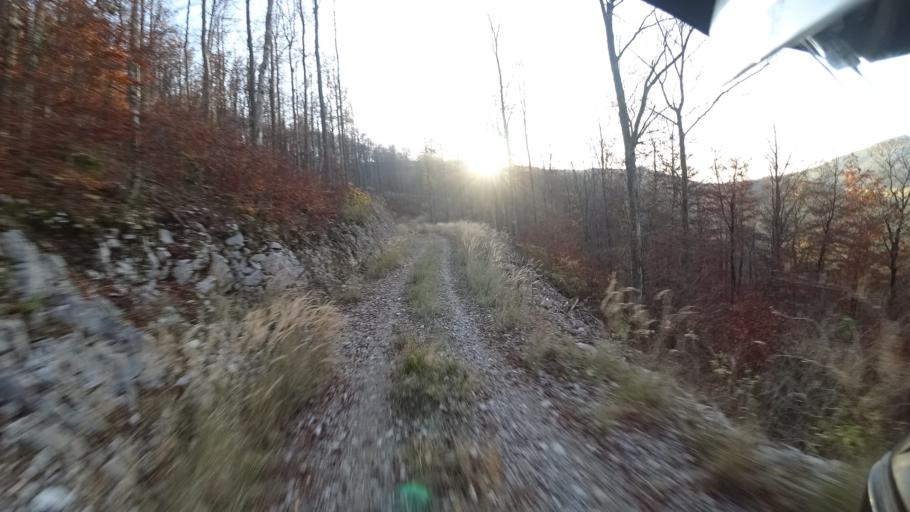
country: HR
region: Primorsko-Goranska
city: Klana
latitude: 45.4946
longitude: 14.4290
